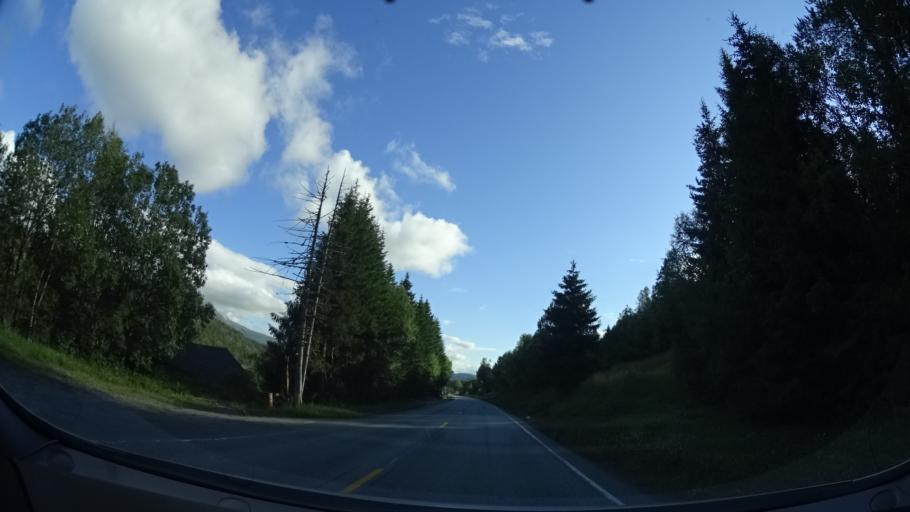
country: NO
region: More og Romsdal
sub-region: Molde
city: Hjelset
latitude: 62.8087
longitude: 7.5843
